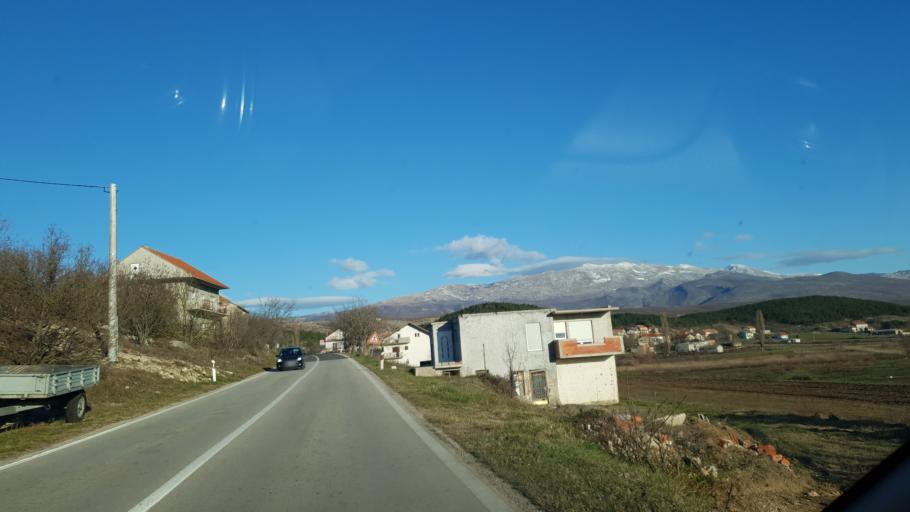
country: HR
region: Splitsko-Dalmatinska
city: Gala
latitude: 43.7258
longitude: 16.6837
